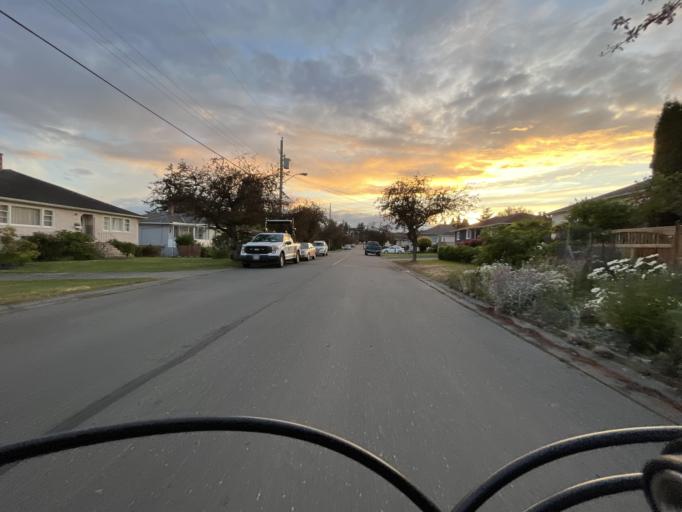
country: CA
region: British Columbia
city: Victoria
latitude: 48.4258
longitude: -123.4111
